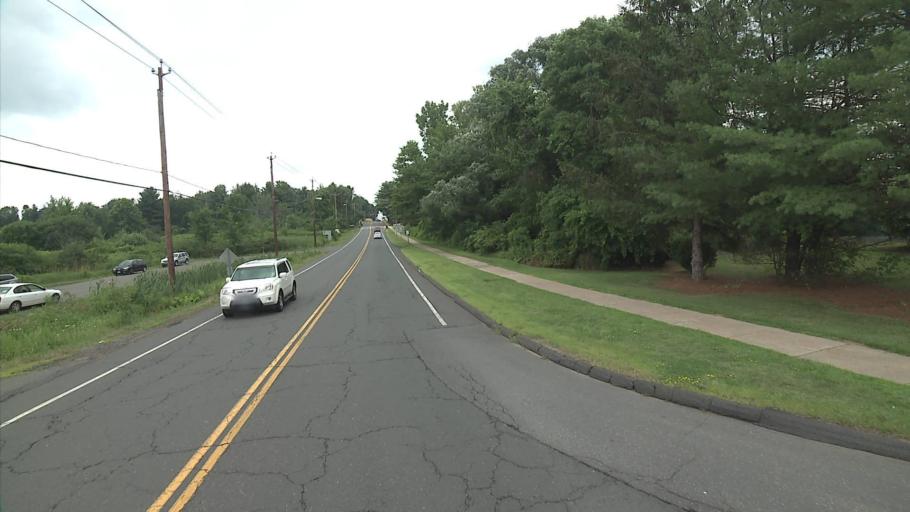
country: US
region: Connecticut
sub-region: Hartford County
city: Newington
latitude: 41.6936
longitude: -72.7325
